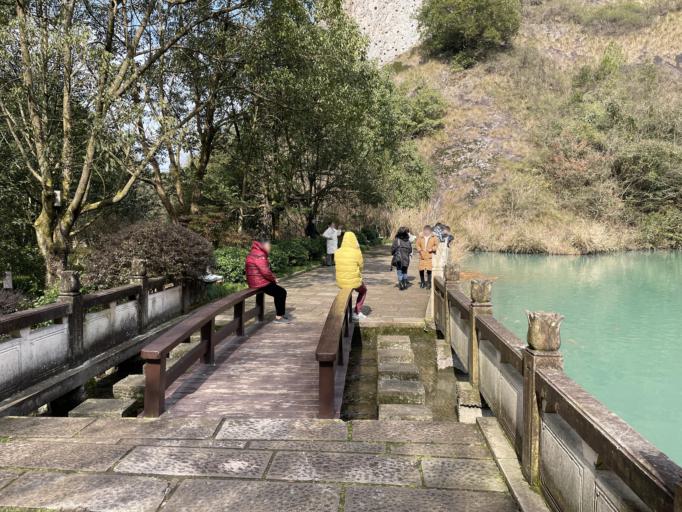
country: CN
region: Zhejiang Sheng
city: Shuhong
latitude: 28.6913
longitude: 120.1388
